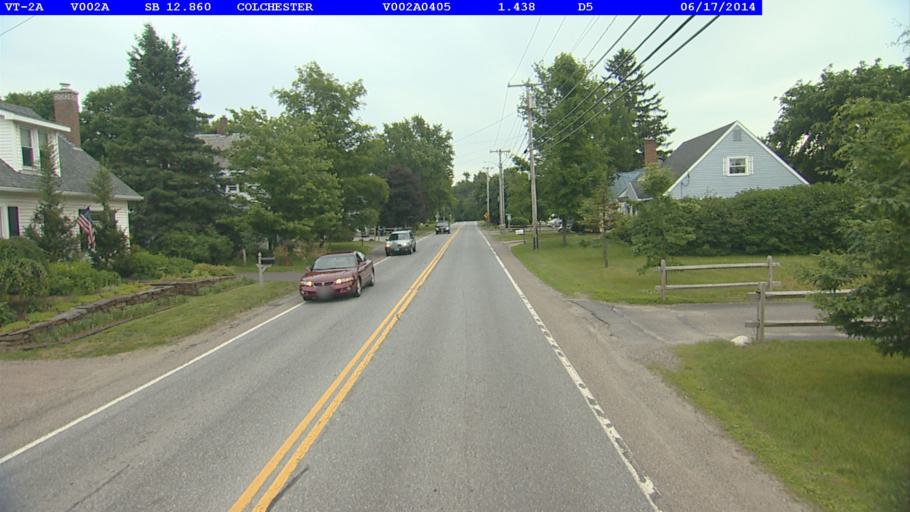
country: US
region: Vermont
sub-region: Chittenden County
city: Colchester
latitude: 44.5432
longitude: -73.1477
